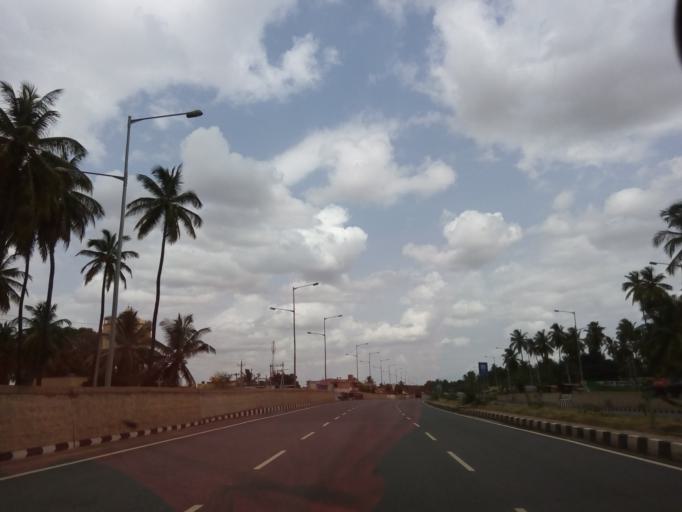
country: IN
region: Karnataka
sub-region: Chitradurga
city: Hiriyur
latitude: 13.9142
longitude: 76.6583
